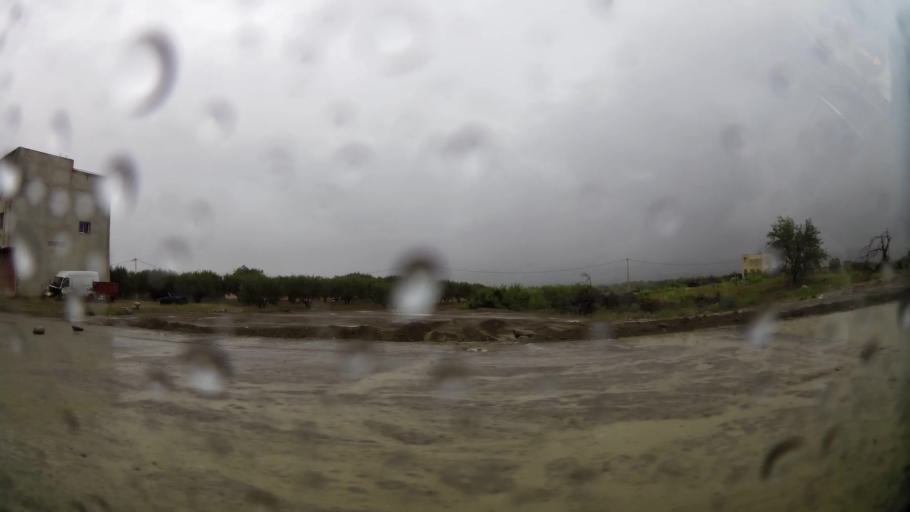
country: MA
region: Oriental
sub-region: Nador
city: Midar
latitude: 34.8694
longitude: -3.7256
